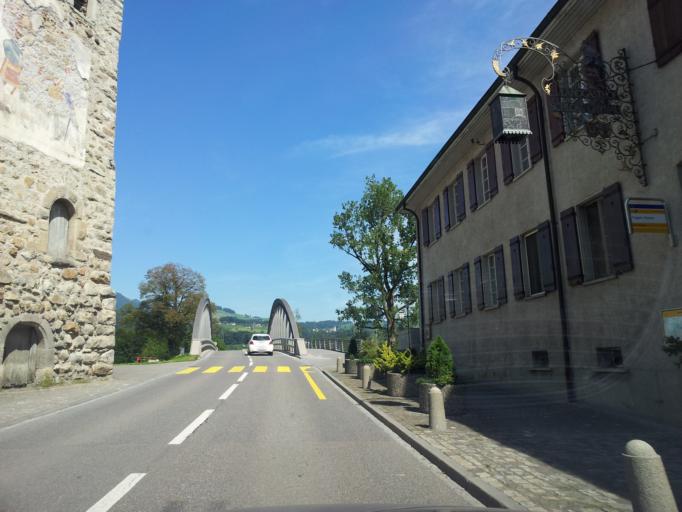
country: CH
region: Saint Gallen
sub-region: Wahlkreis See-Gaster
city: Uznach
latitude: 47.2163
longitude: 8.9702
